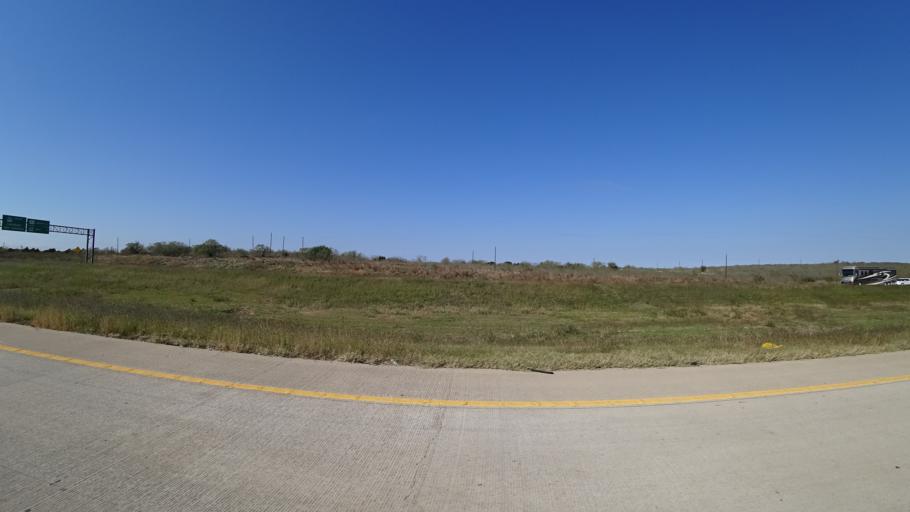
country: US
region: Texas
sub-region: Travis County
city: Onion Creek
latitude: 30.1053
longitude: -97.6669
